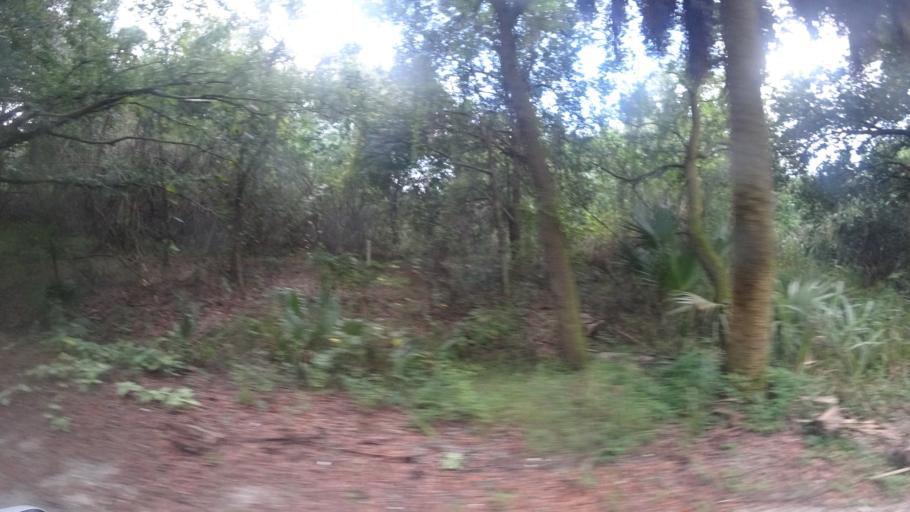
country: US
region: Florida
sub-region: Manatee County
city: Memphis
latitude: 27.6173
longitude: -82.5150
